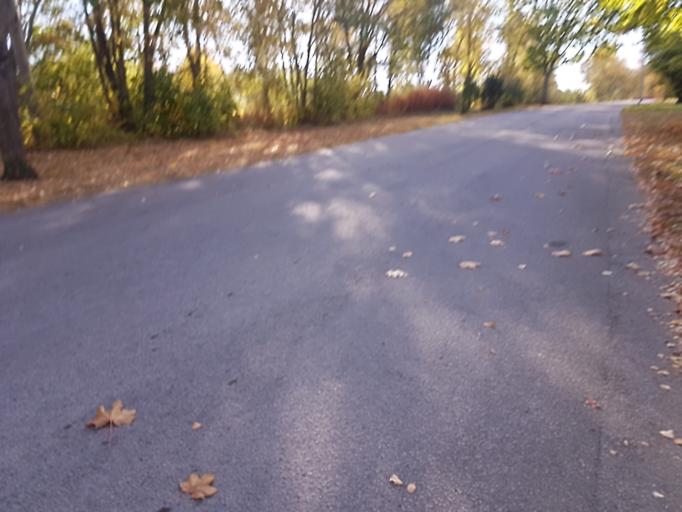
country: SE
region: Kronoberg
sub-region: Vaxjo Kommun
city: Vaexjoe
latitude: 56.8469
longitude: 14.8231
